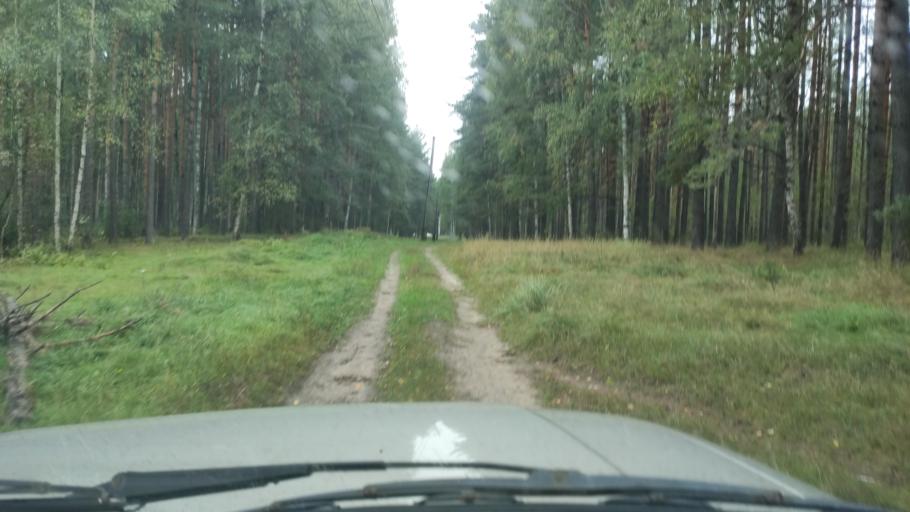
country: RU
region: Nizjnij Novgorod
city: Taremskoye
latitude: 56.0022
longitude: 42.9842
